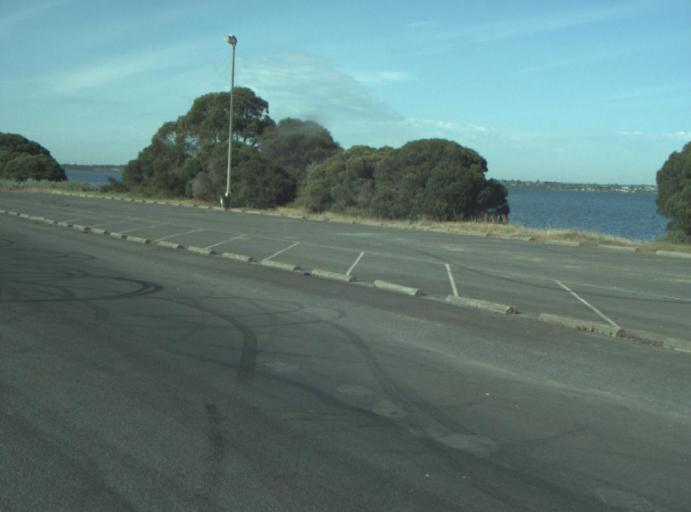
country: AU
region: Victoria
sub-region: Greater Geelong
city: East Geelong
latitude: -38.1368
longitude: 144.4203
